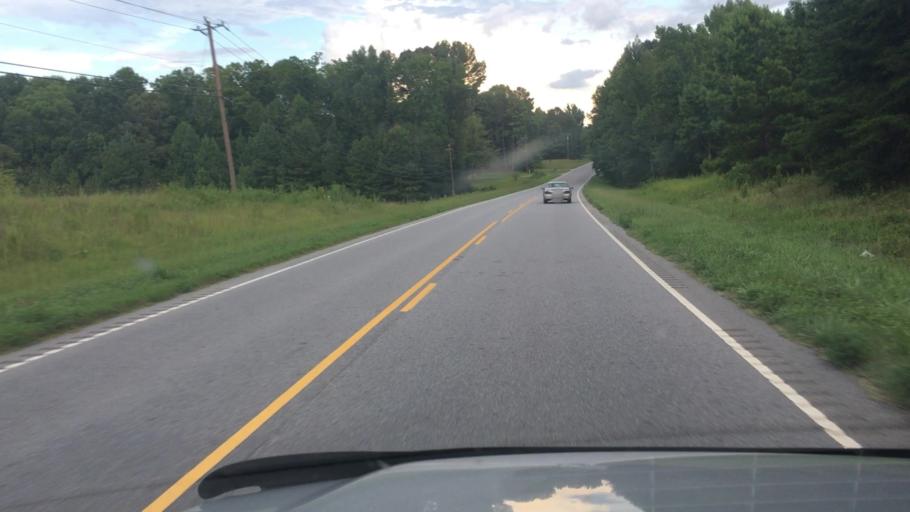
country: US
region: South Carolina
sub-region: Spartanburg County
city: Mayo
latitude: 35.1405
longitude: -81.8122
